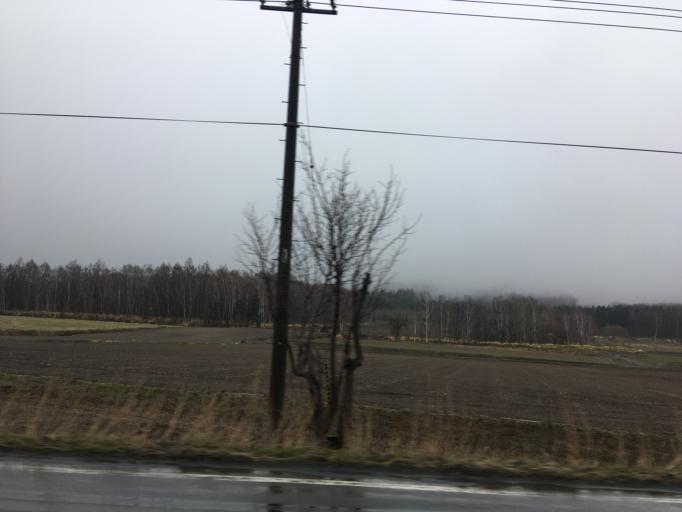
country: JP
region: Hokkaido
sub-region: Asahikawa-shi
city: Asahikawa
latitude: 43.9992
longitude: 142.4408
